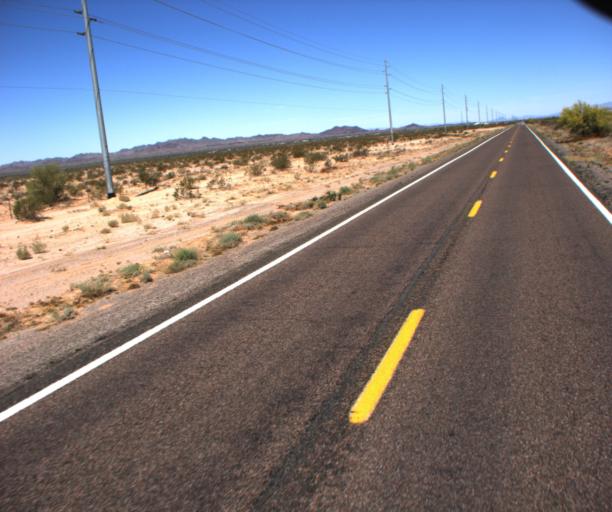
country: US
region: Arizona
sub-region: La Paz County
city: Quartzsite
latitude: 33.8944
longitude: -113.9646
